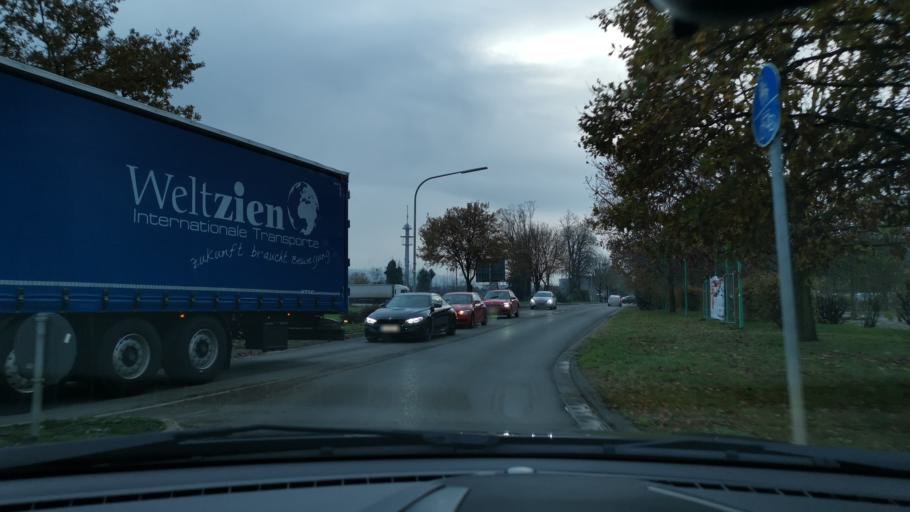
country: DE
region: North Rhine-Westphalia
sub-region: Regierungsbezirk Dusseldorf
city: Grevenbroich
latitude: 51.0952
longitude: 6.6077
